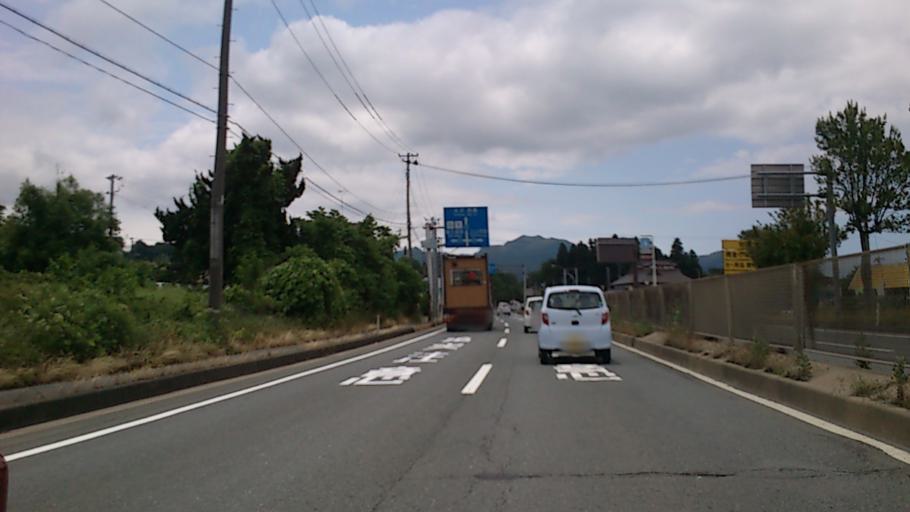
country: JP
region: Yamagata
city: Kaminoyama
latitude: 38.1853
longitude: 140.3098
